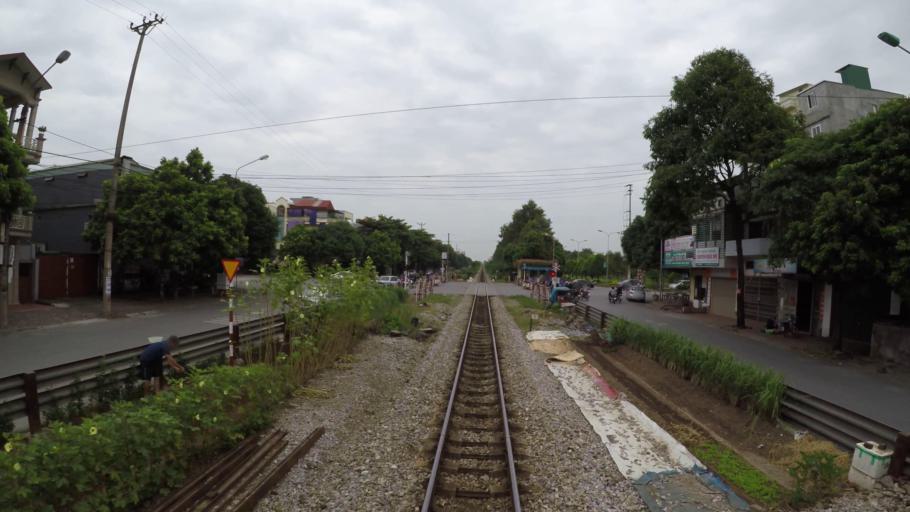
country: VN
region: Hai Duong
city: Thanh Pho Hai Duong
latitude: 20.9443
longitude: 106.3507
